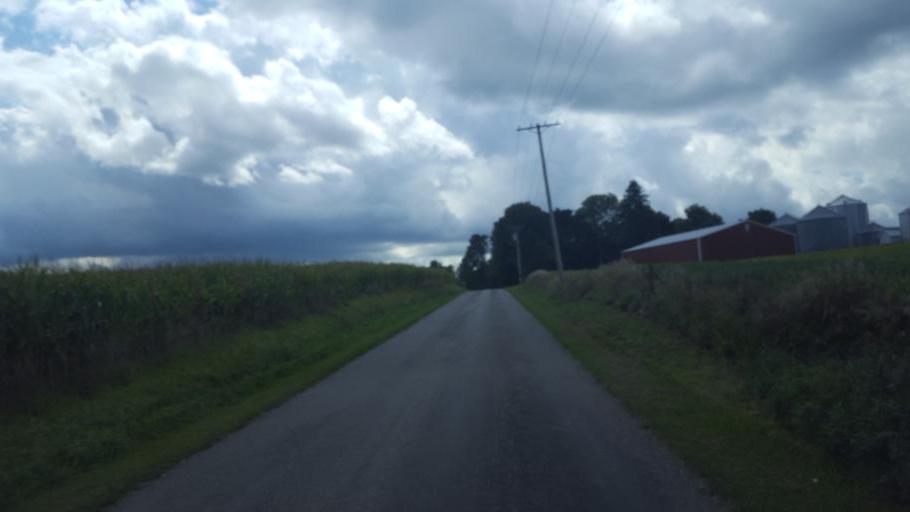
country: US
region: Ohio
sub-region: Huron County
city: Willard
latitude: 41.1063
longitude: -82.6323
